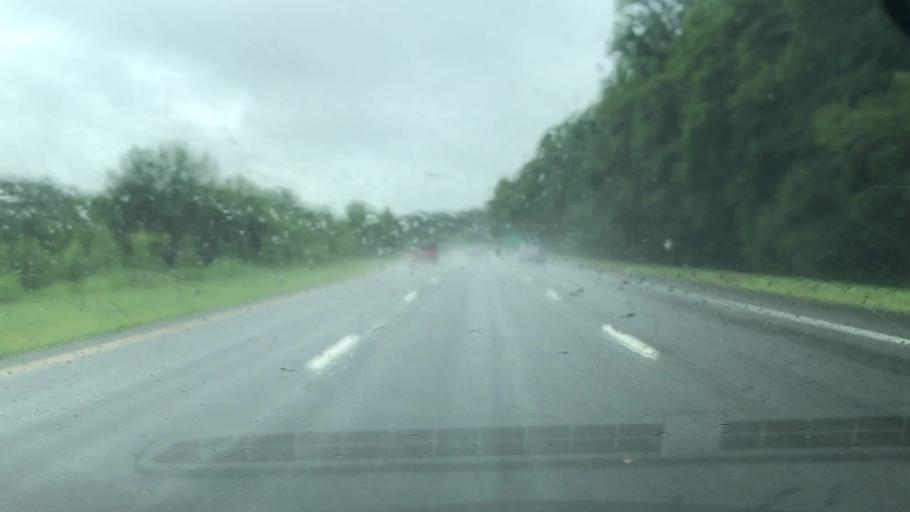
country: US
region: New York
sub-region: Westchester County
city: Yorktown Heights
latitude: 41.2491
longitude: -73.8111
